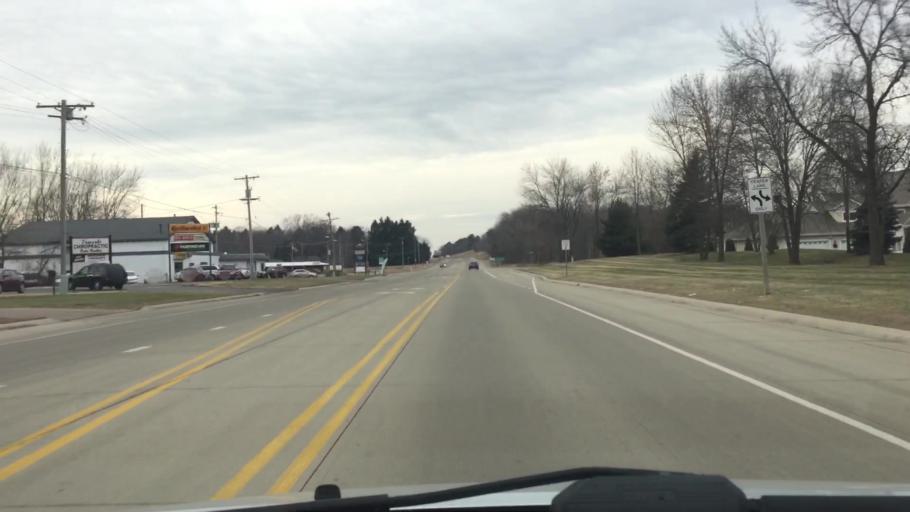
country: US
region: Wisconsin
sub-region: Waukesha County
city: Oconomowoc
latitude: 43.1270
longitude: -88.5351
